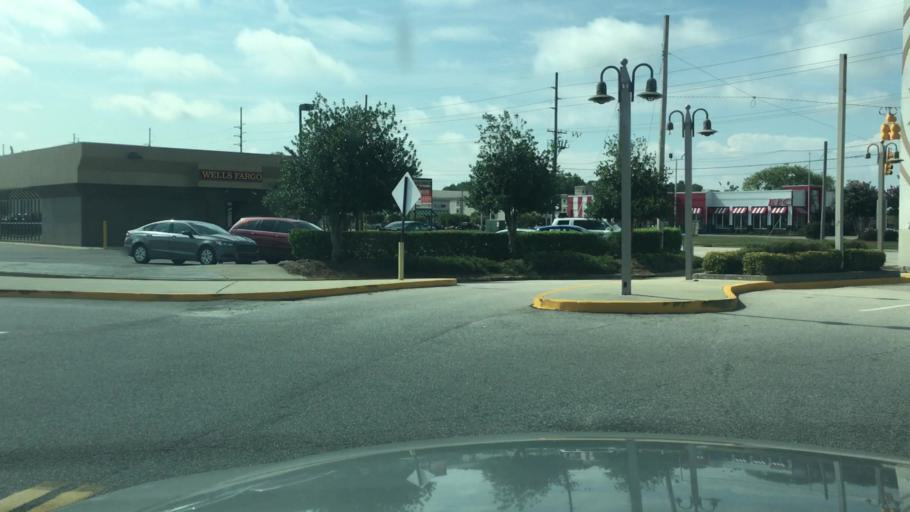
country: US
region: North Carolina
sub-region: Cumberland County
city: Fort Bragg
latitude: 35.0706
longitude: -78.9628
